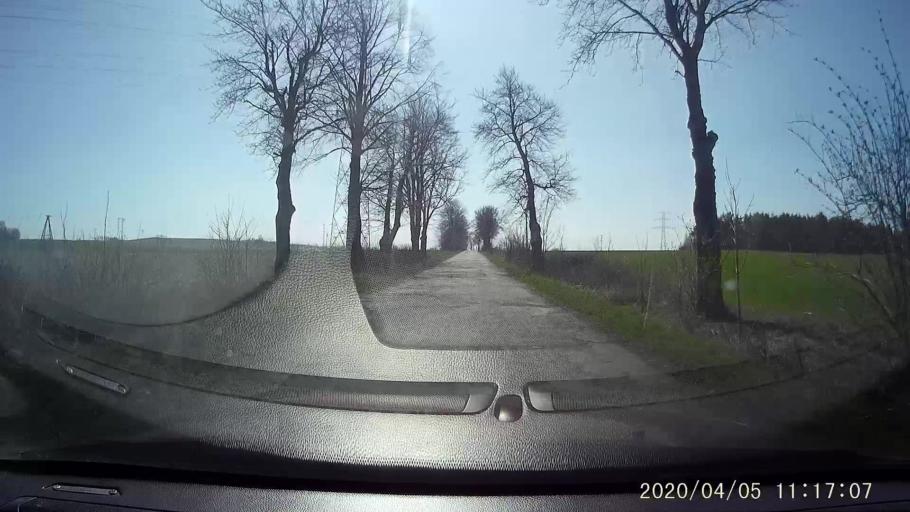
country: PL
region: Lower Silesian Voivodeship
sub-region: Powiat zgorzelecki
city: Sulikow
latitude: 51.0742
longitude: 15.1040
